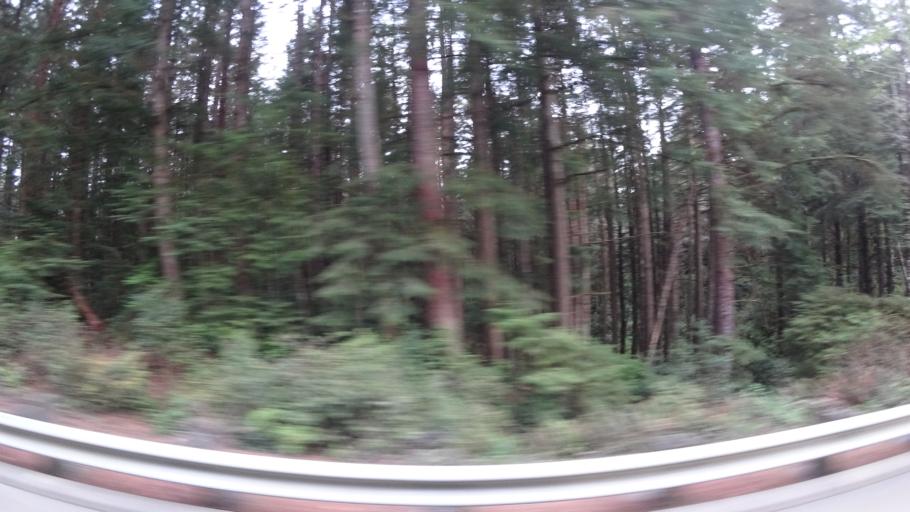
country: US
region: Oregon
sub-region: Coos County
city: Coquille
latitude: 43.2260
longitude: -124.2993
